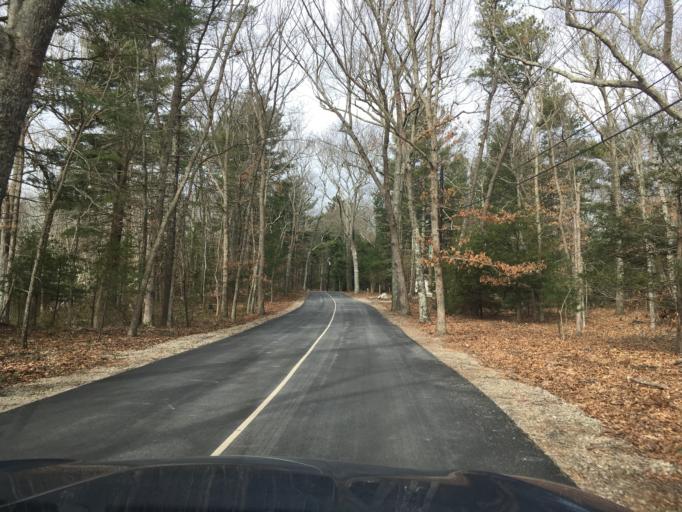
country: US
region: Rhode Island
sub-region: Kent County
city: East Greenwich
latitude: 41.6484
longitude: -71.4270
